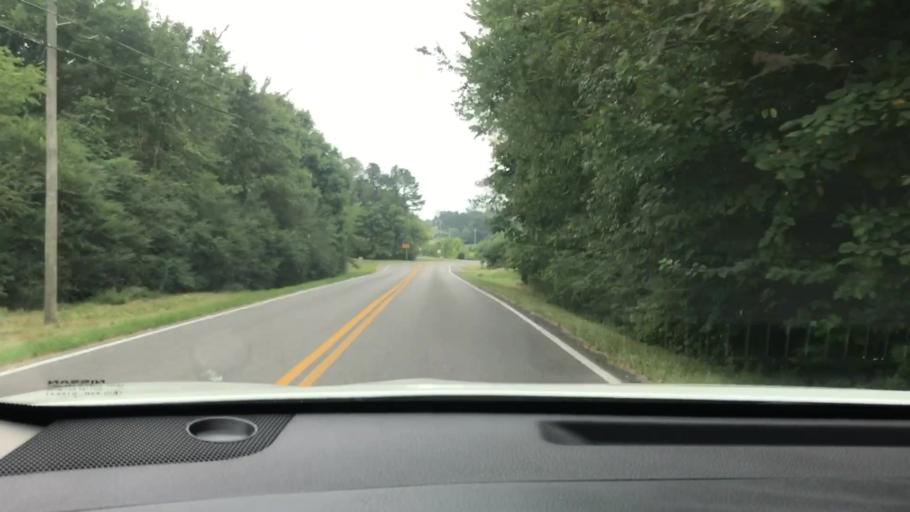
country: US
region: Kentucky
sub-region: Calloway County
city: Murray
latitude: 36.6782
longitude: -88.3013
